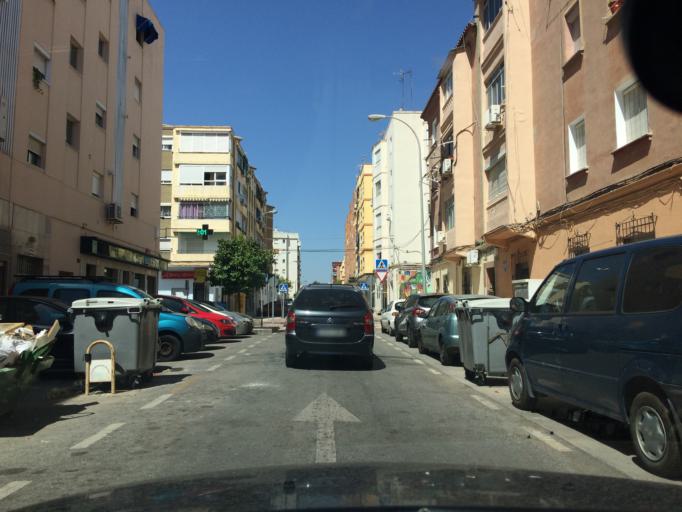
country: ES
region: Andalusia
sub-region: Provincia de Malaga
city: Malaga
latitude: 36.7098
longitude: -4.4486
